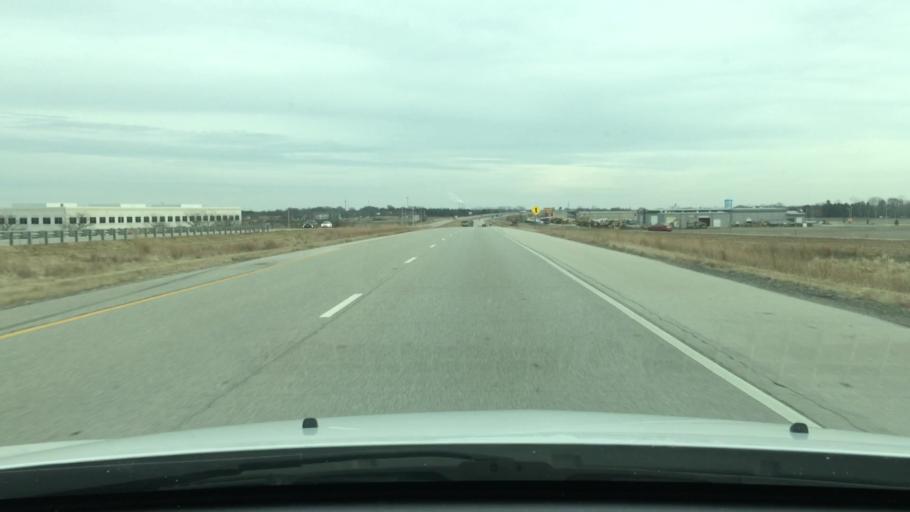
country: US
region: Illinois
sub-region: Sangamon County
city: Jerome
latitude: 39.7518
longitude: -89.7500
